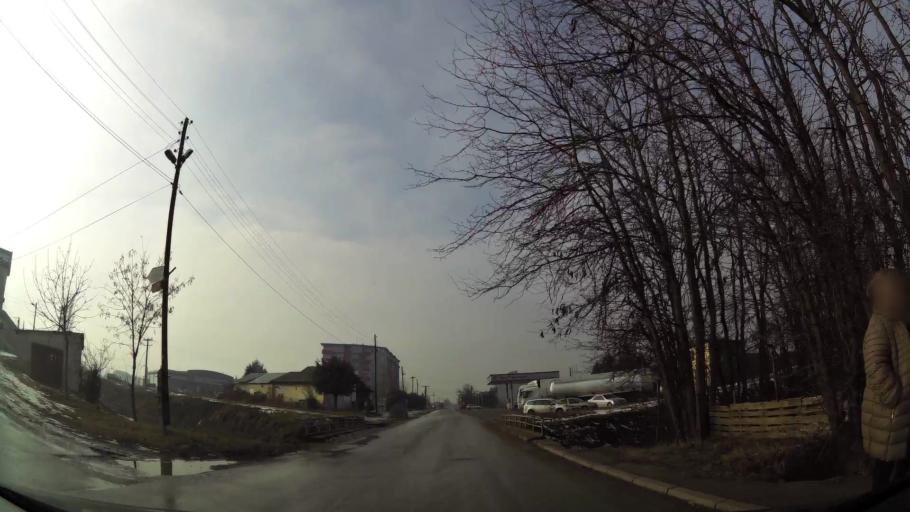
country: MK
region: Ilinden
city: Marino
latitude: 41.9903
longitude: 21.5879
